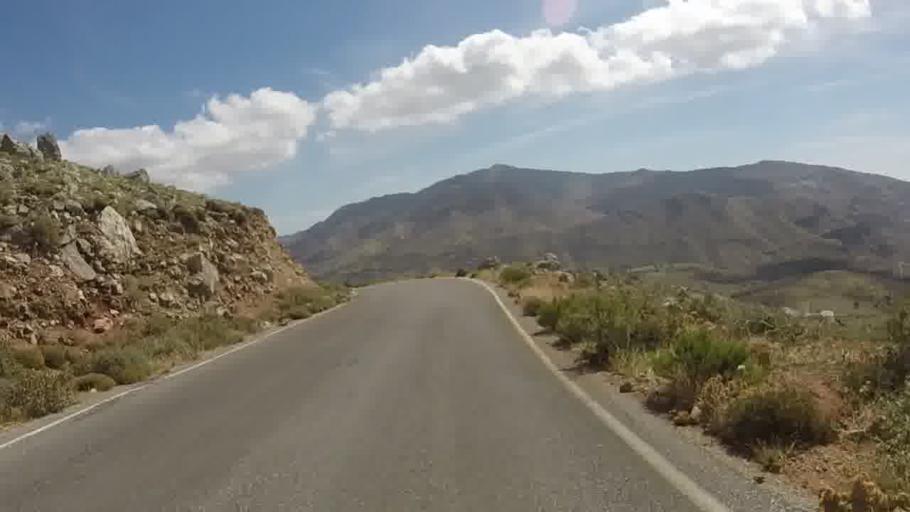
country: GR
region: Crete
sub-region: Nomos Rethymnis
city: Agia Galini
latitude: 35.1566
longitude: 24.6168
